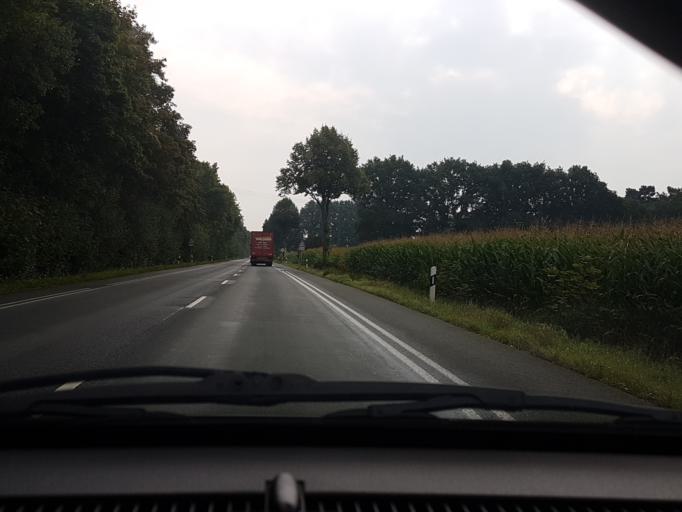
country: DE
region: North Rhine-Westphalia
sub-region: Regierungsbezirk Munster
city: Neuenkirchen
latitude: 52.1867
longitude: 7.4286
